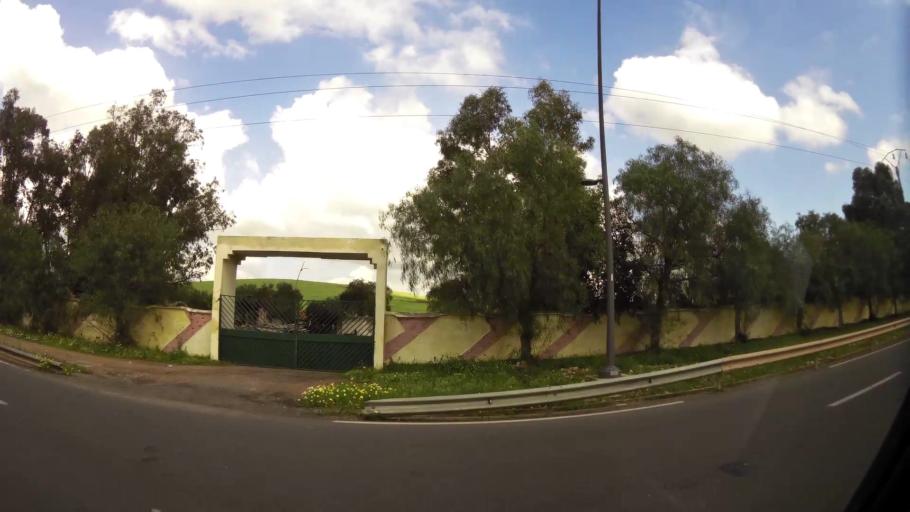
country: MA
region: Chaouia-Ouardigha
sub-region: Settat Province
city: Settat
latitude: 33.0579
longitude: -7.6262
